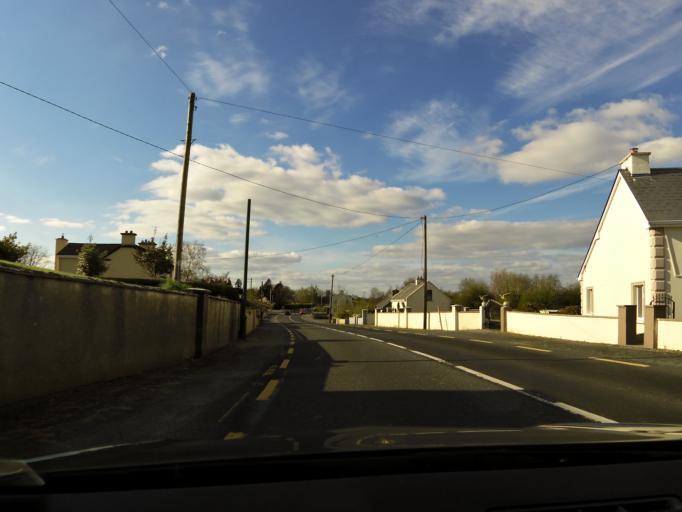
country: IE
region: Connaught
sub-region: County Galway
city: Portumna
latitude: 53.1044
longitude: -8.2345
